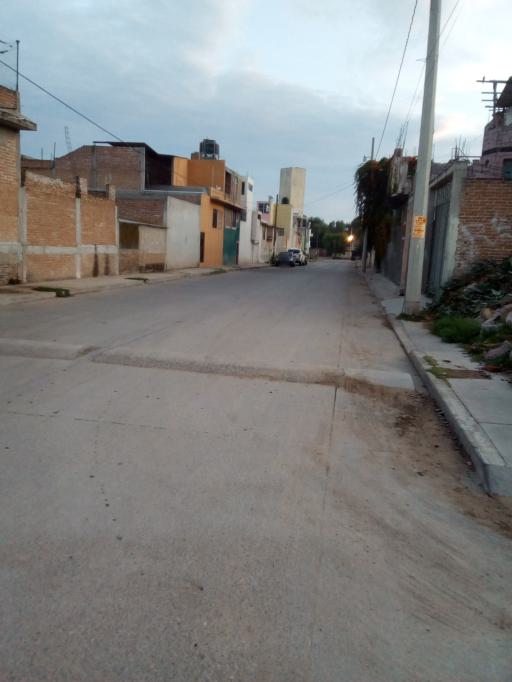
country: MX
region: Guerrero
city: San Luis de la Paz
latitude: 21.2863
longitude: -100.5232
